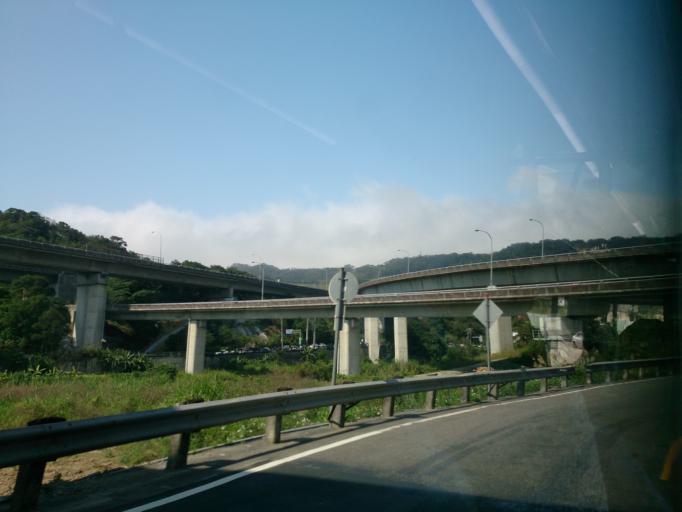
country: TW
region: Taipei
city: Taipei
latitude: 25.0021
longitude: 121.5964
